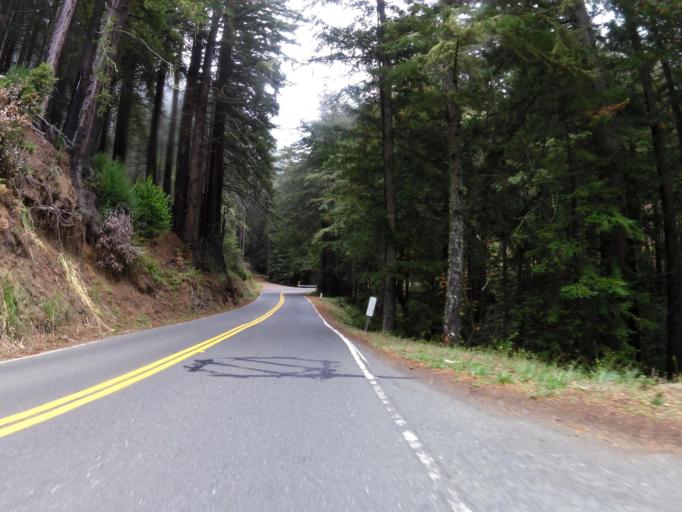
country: US
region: California
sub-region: Sonoma County
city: Monte Rio
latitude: 38.5011
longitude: -123.2093
